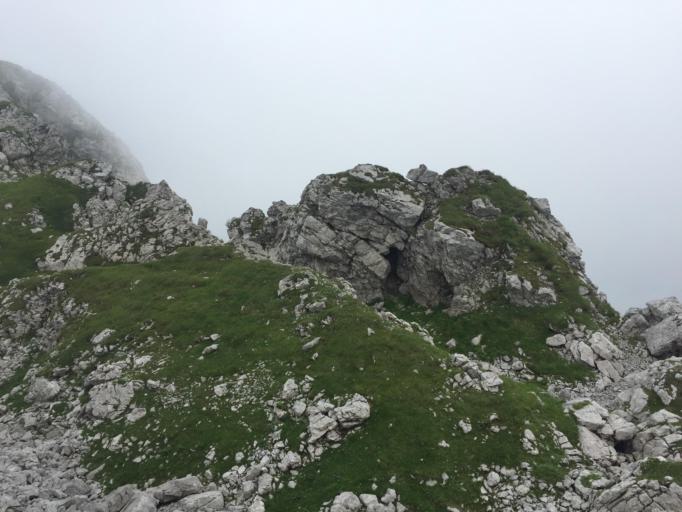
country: IT
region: Friuli Venezia Giulia
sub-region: Provincia di Udine
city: Pontebba
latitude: 46.5493
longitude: 13.2247
